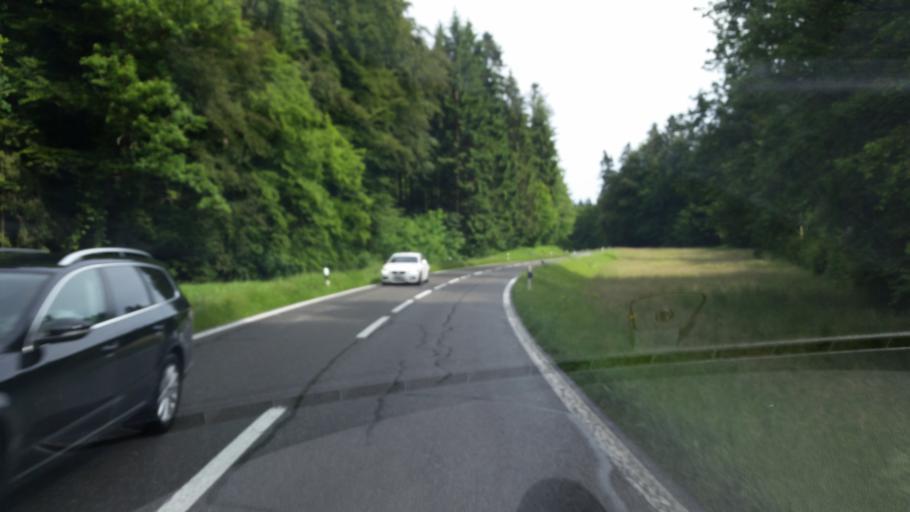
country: CH
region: Aargau
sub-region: Bezirk Bremgarten
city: Bremgarten
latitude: 47.3222
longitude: 8.3503
